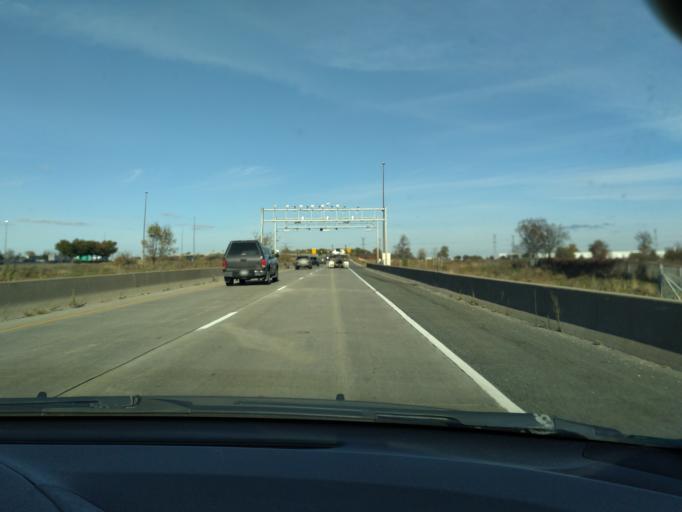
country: CA
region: Ontario
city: Brampton
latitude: 43.5925
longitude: -79.8040
